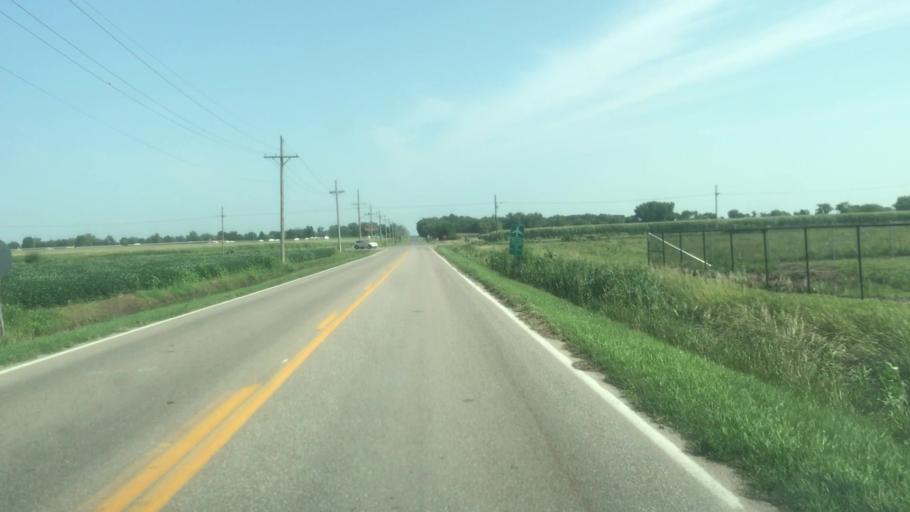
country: US
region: Nebraska
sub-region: Hall County
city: Grand Island
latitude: 40.9437
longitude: -98.3015
